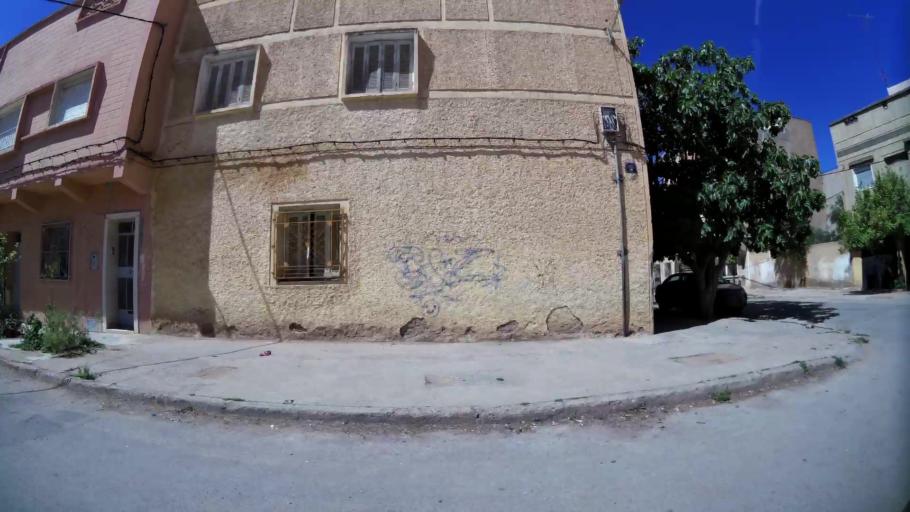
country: MA
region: Oriental
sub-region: Oujda-Angad
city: Oujda
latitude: 34.6710
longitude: -1.9303
